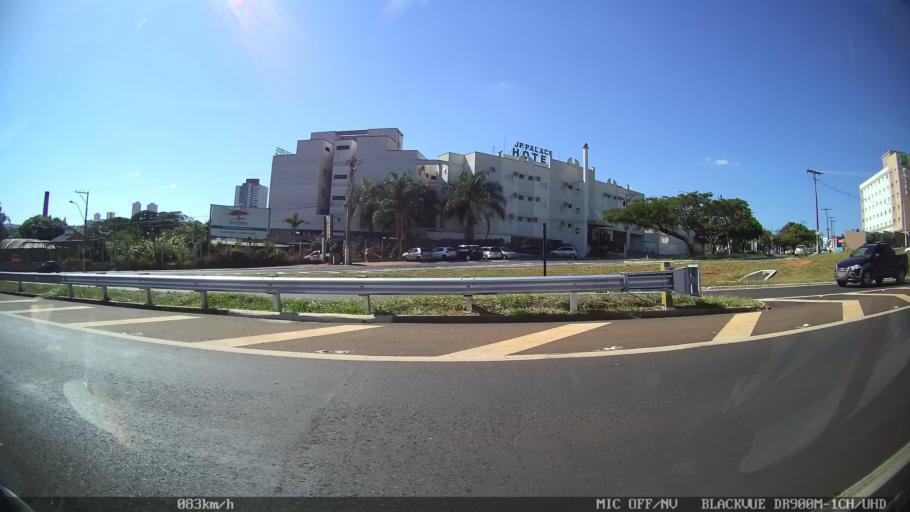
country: BR
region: Sao Paulo
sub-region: Franca
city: Franca
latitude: -20.5556
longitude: -47.4089
